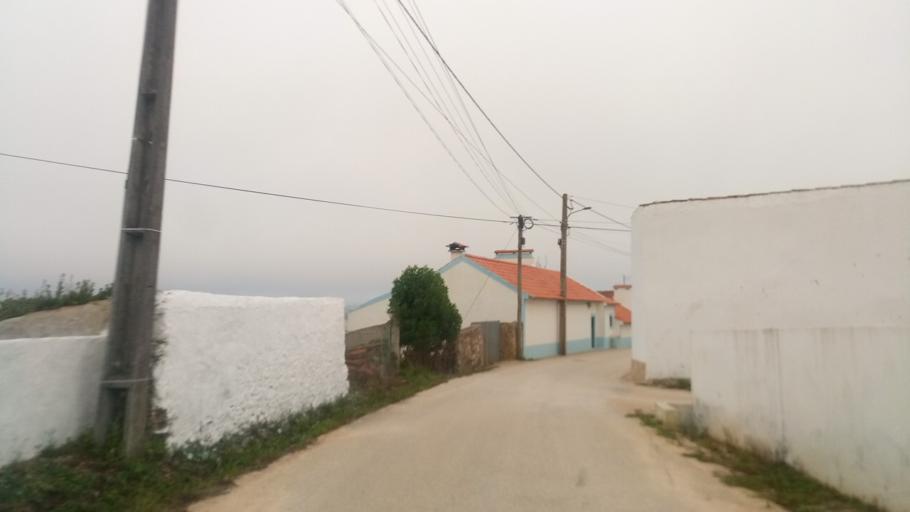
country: PT
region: Leiria
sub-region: Caldas da Rainha
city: Caldas da Rainha
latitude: 39.4621
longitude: -9.1934
